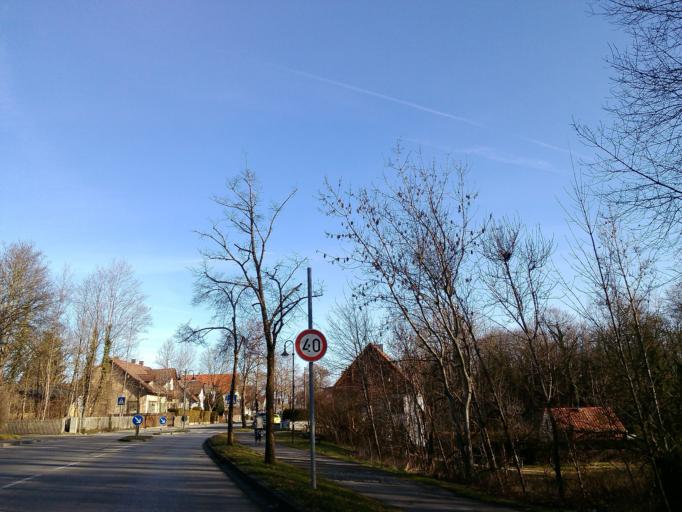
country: DE
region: Bavaria
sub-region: Upper Bavaria
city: Emmering
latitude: 48.1827
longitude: 11.2693
